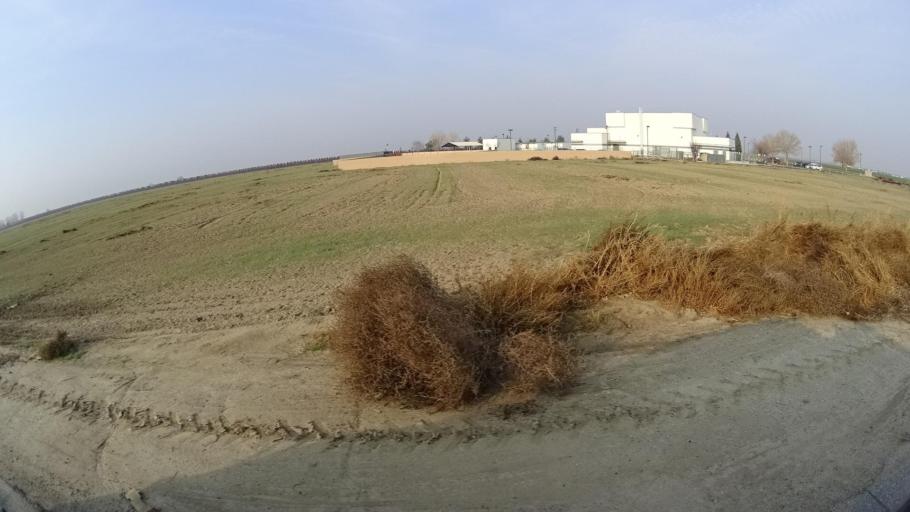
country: US
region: California
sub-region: Kern County
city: Greenfield
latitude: 35.2216
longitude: -119.0213
